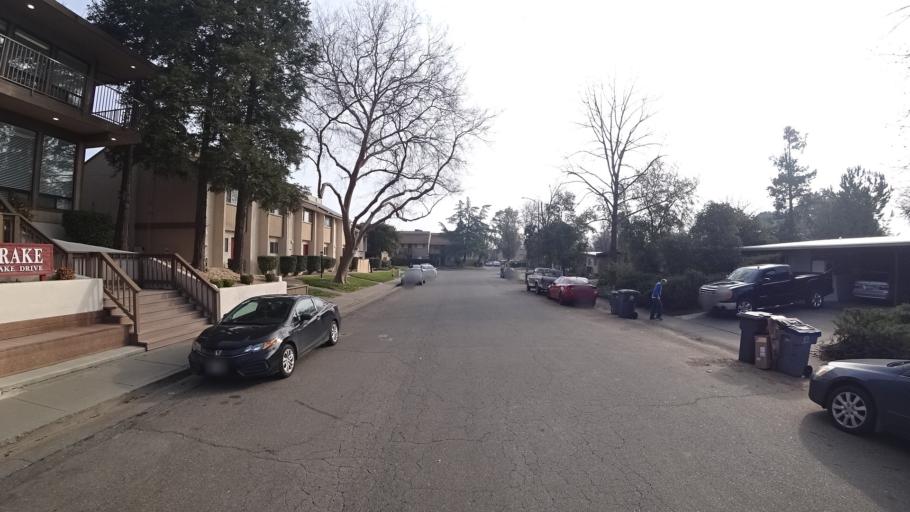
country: US
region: California
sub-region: Yolo County
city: Davis
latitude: 38.5601
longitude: -121.7614
